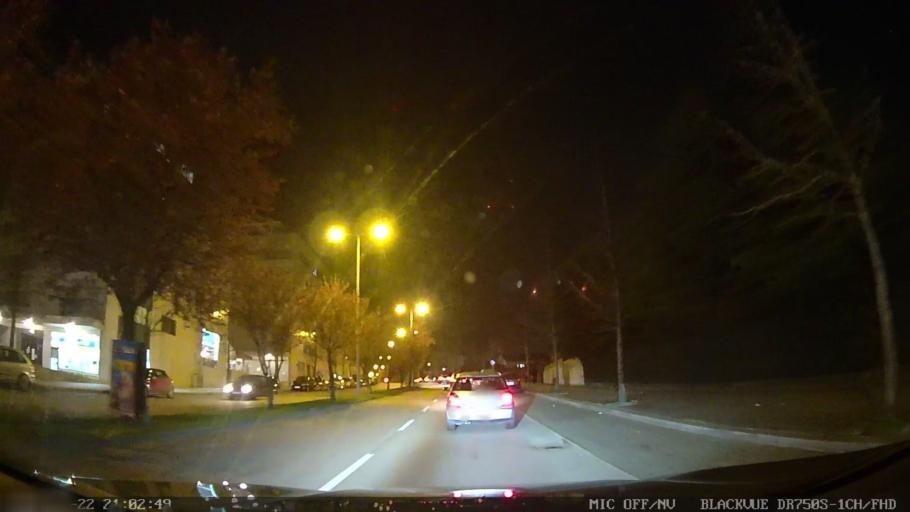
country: PT
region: Porto
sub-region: Matosinhos
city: Senhora da Hora
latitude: 41.1900
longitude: -8.6352
